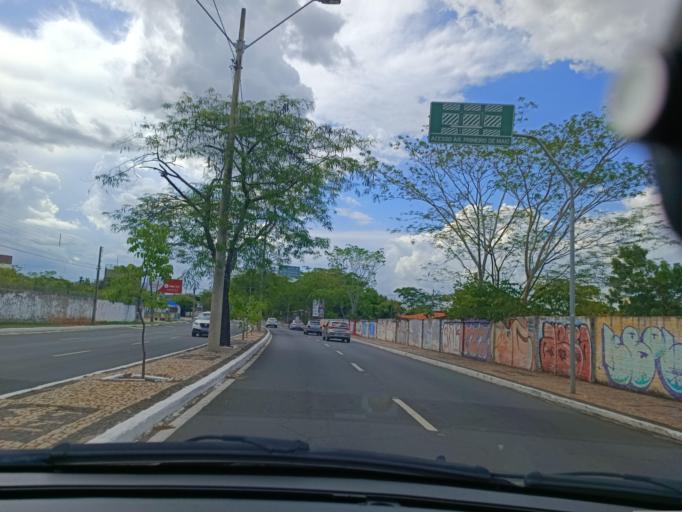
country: BR
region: Piaui
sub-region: Teresina
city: Teresina
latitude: -5.0817
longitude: -42.8066
